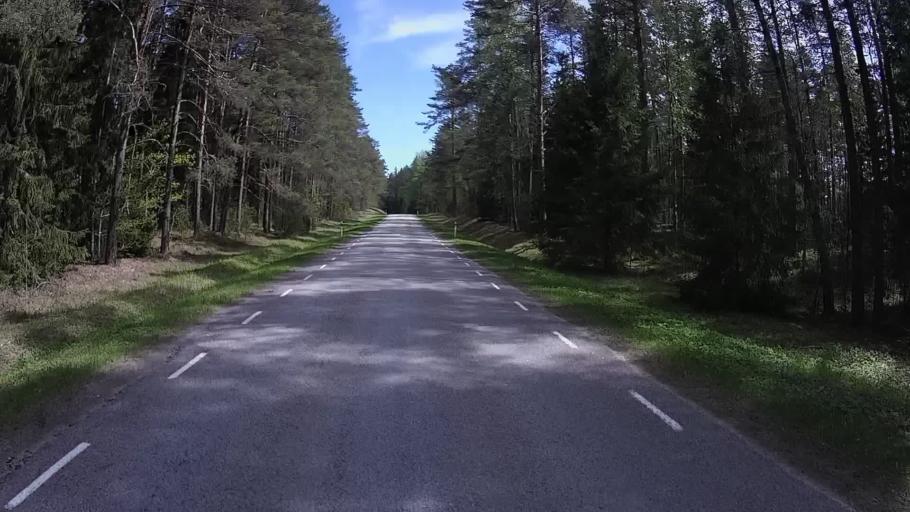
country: LV
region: Apes Novads
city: Ape
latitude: 57.6056
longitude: 26.4665
